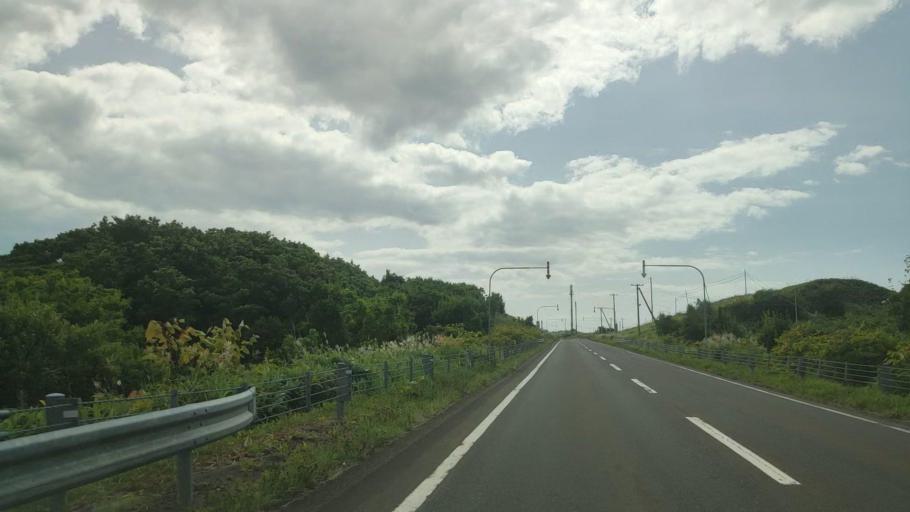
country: JP
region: Hokkaido
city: Rumoi
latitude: 44.6035
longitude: 141.7940
